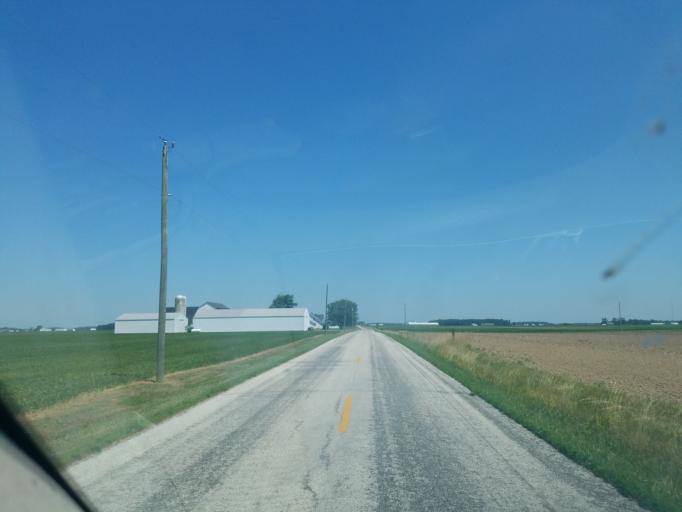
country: US
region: Ohio
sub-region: Mercer County
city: Rockford
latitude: 40.6225
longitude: -84.7085
